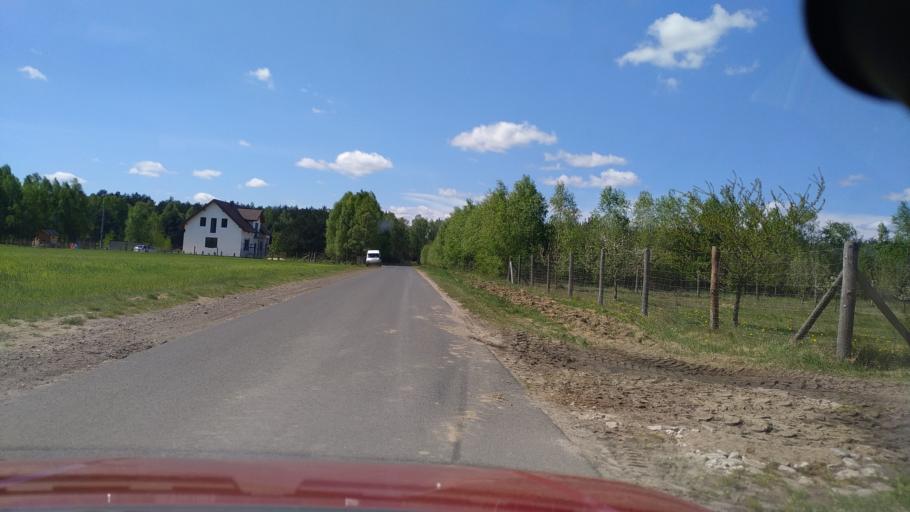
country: PL
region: Greater Poland Voivodeship
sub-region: Powiat zlotowski
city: Tarnowka
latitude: 53.2650
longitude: 16.8997
